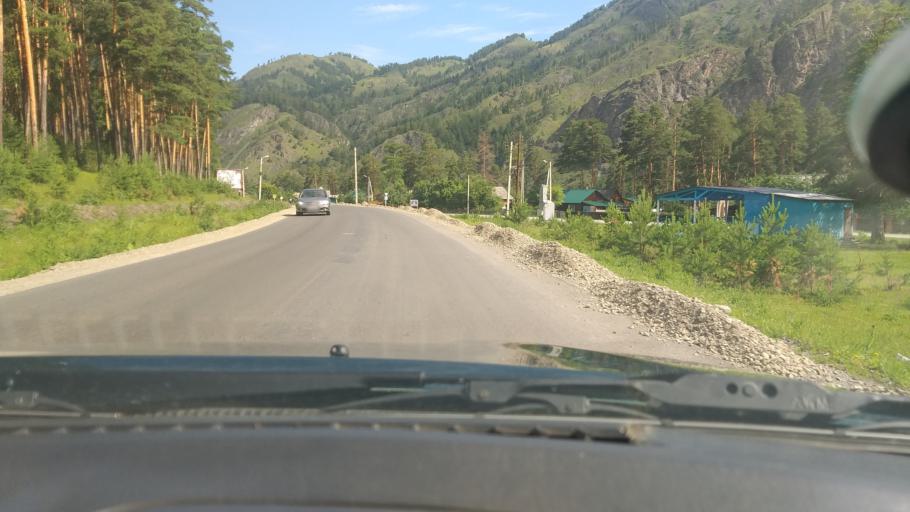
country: RU
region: Altay
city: Chemal
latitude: 51.3974
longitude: 86.0232
